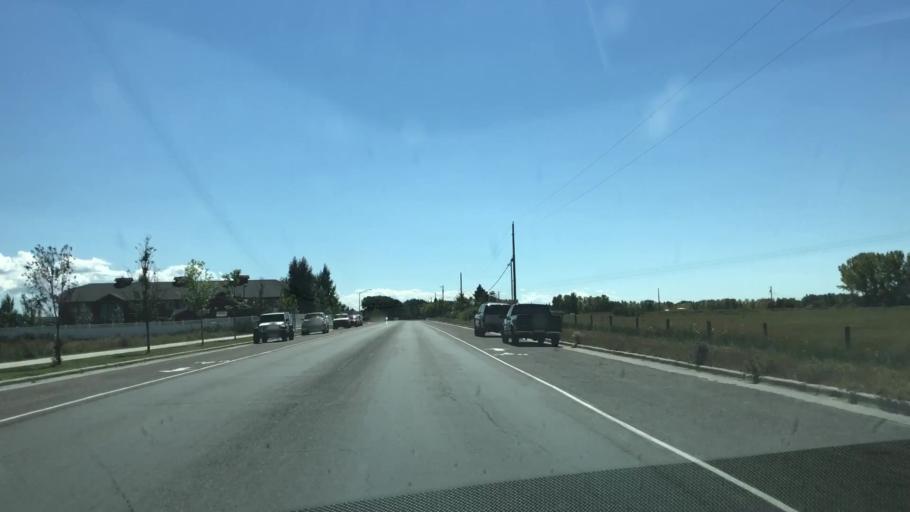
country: US
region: Wyoming
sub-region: Albany County
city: Laramie
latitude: 41.3264
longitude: -105.6203
